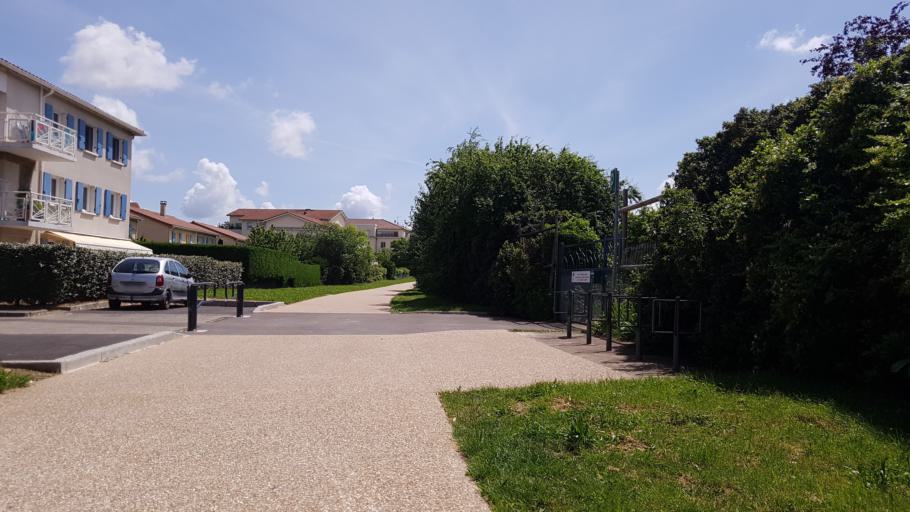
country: FR
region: Rhone-Alpes
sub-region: Departement du Rhone
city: Sathonay-Village
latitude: 45.8184
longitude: 4.8834
